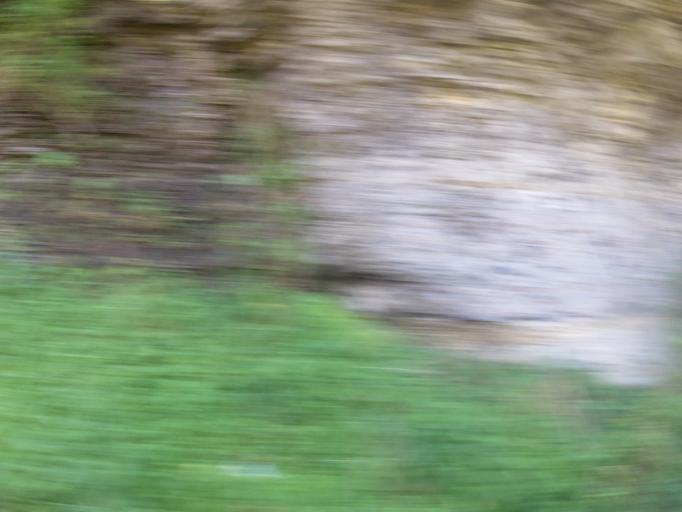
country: US
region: Kentucky
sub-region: Leslie County
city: Hyden
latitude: 37.1627
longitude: -83.5619
